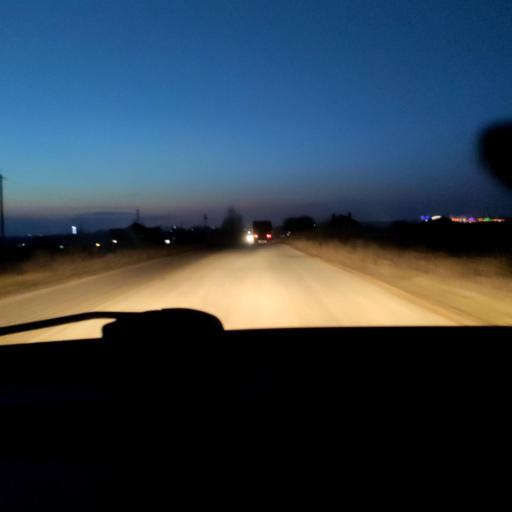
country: RU
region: Bashkortostan
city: Ufa
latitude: 54.7048
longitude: 56.1131
